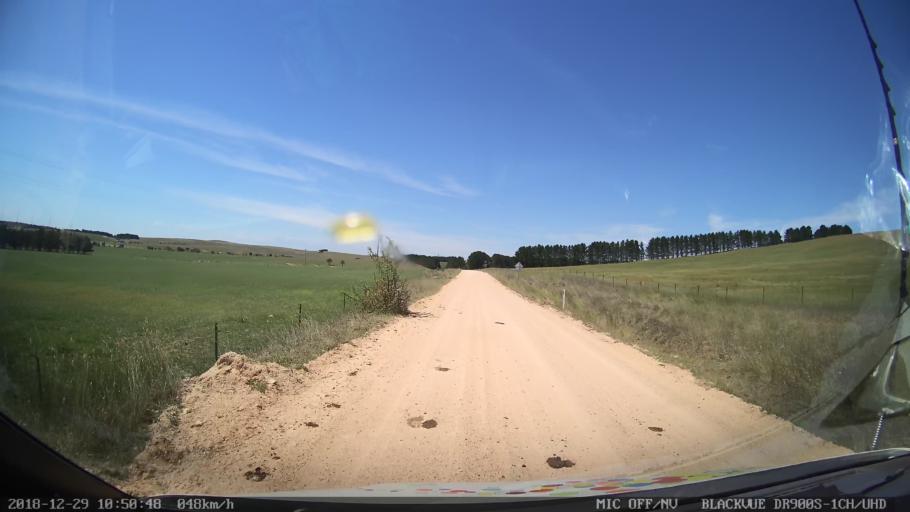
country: AU
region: New South Wales
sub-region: Palerang
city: Bungendore
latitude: -35.0842
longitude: 149.5241
